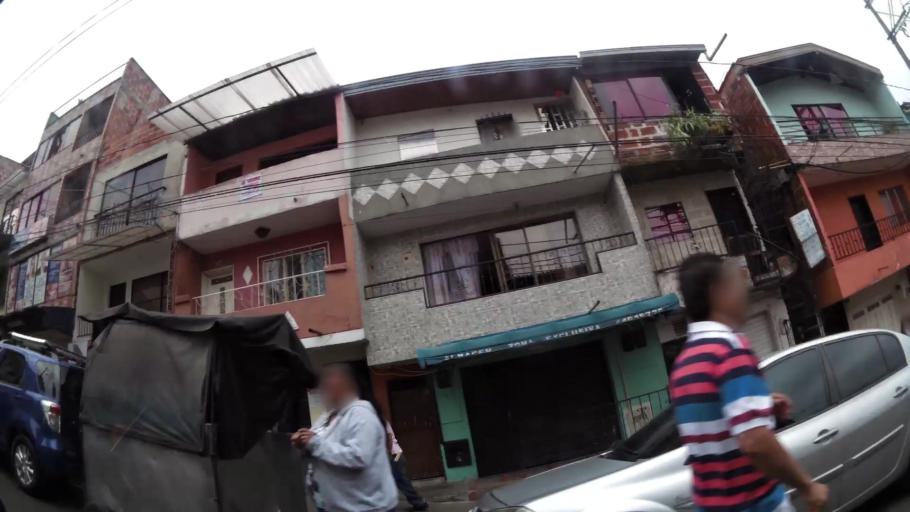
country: CO
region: Antioquia
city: Bello
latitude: 6.3063
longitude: -75.5535
